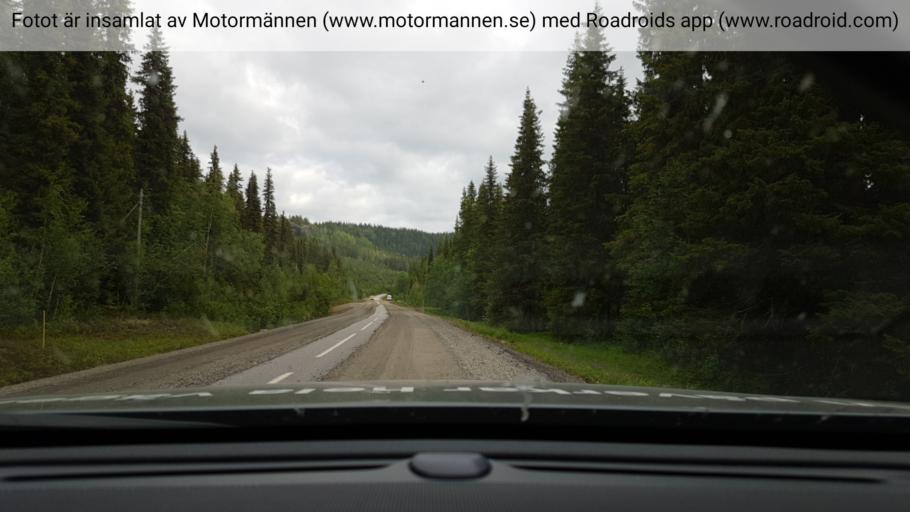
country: SE
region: Vaesterbotten
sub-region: Storumans Kommun
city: Fristad
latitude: 65.8186
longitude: 16.8160
